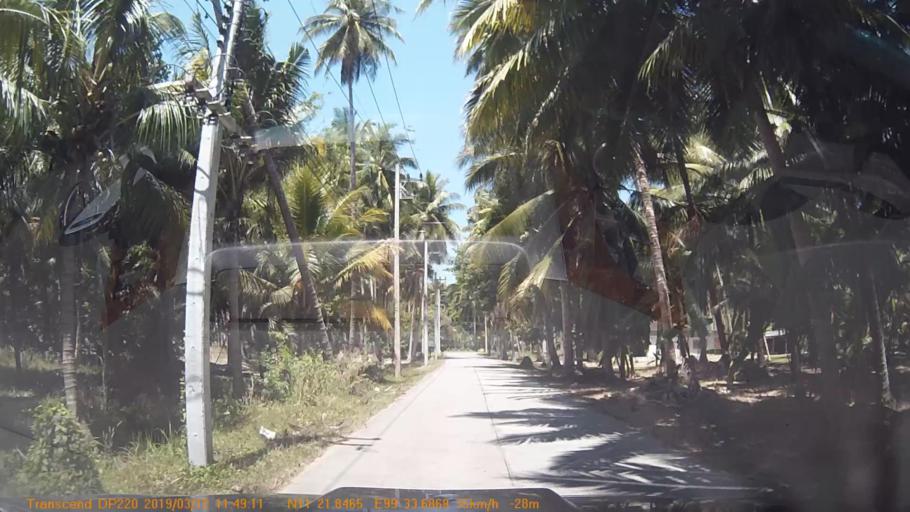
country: TH
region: Prachuap Khiri Khan
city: Thap Sakae
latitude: 11.3642
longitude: 99.5613
